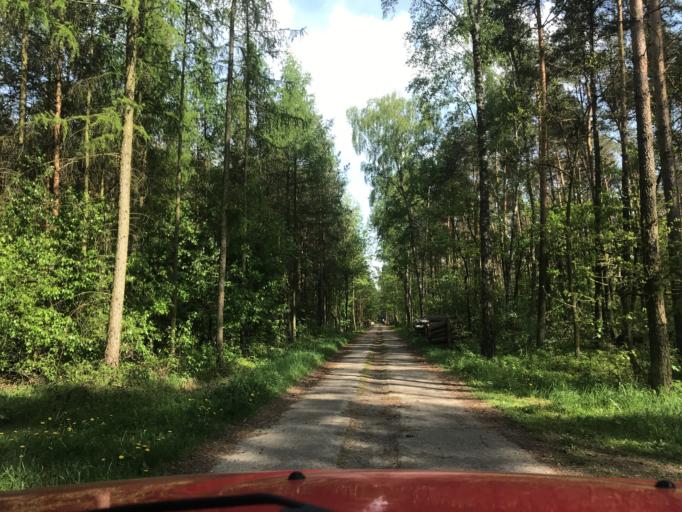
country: PL
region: Greater Poland Voivodeship
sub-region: Powiat kaliski
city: Stawiszyn
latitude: 51.9412
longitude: 18.1547
